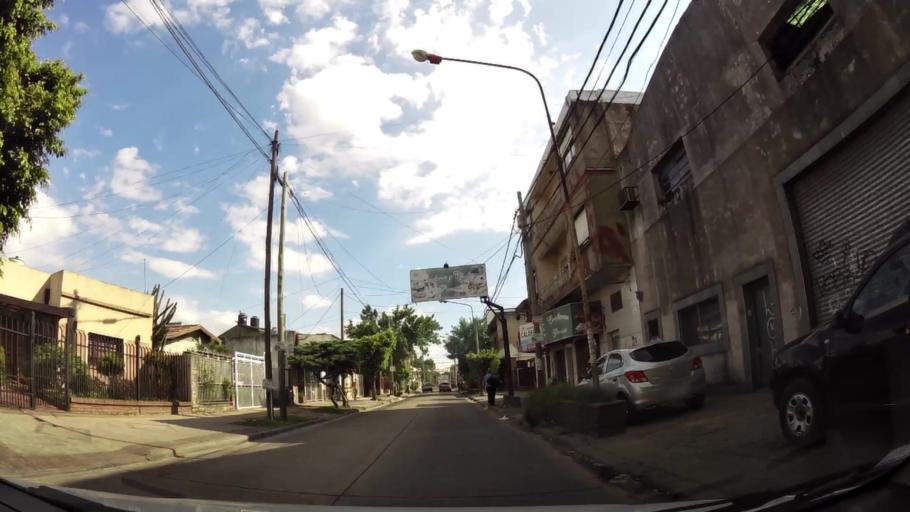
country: AR
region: Buenos Aires
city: San Justo
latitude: -34.6517
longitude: -58.5766
